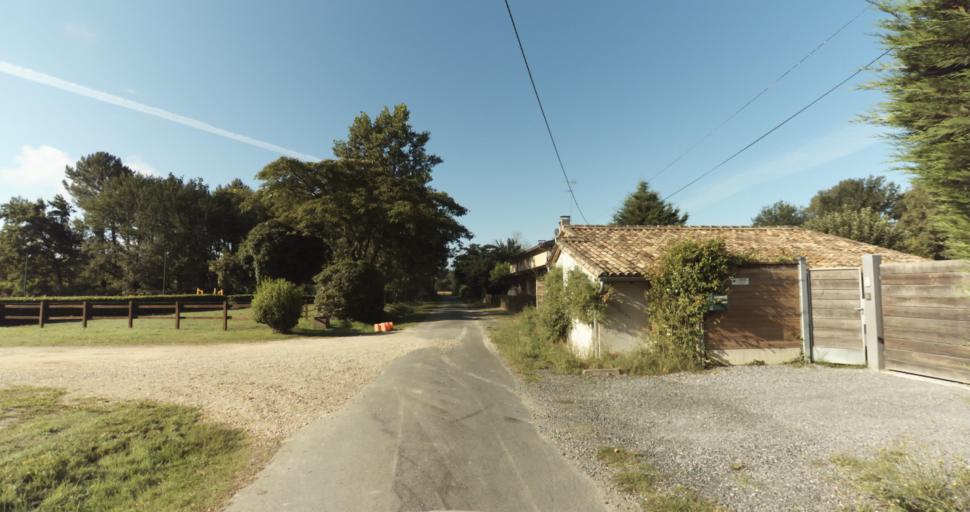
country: FR
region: Aquitaine
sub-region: Departement de la Gironde
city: Bazas
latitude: 44.4442
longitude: -0.2622
